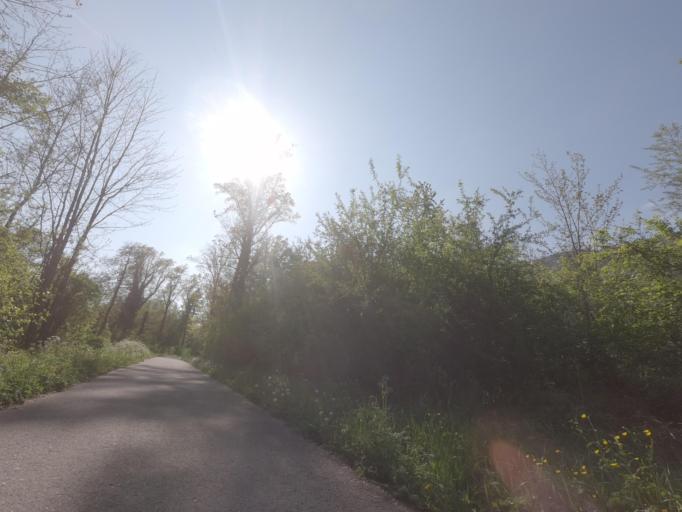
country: CH
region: Bern
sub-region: Biel/Bienne District
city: Orpund
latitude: 47.1656
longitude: 7.3071
